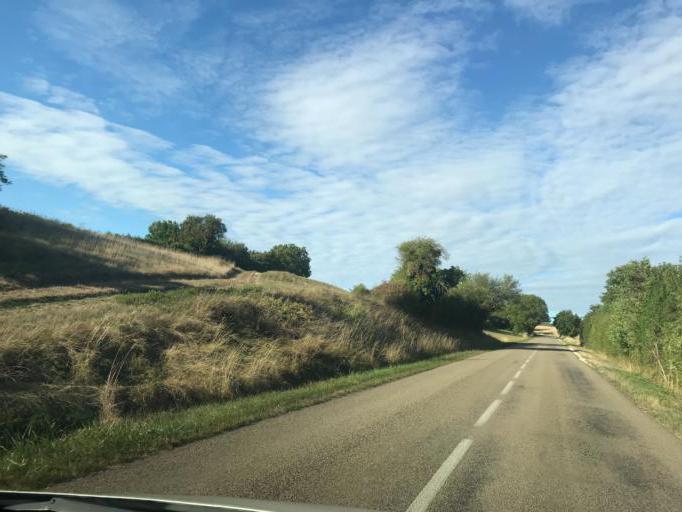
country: FR
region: Bourgogne
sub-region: Departement de l'Yonne
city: Fontenailles
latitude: 47.5525
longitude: 3.4284
